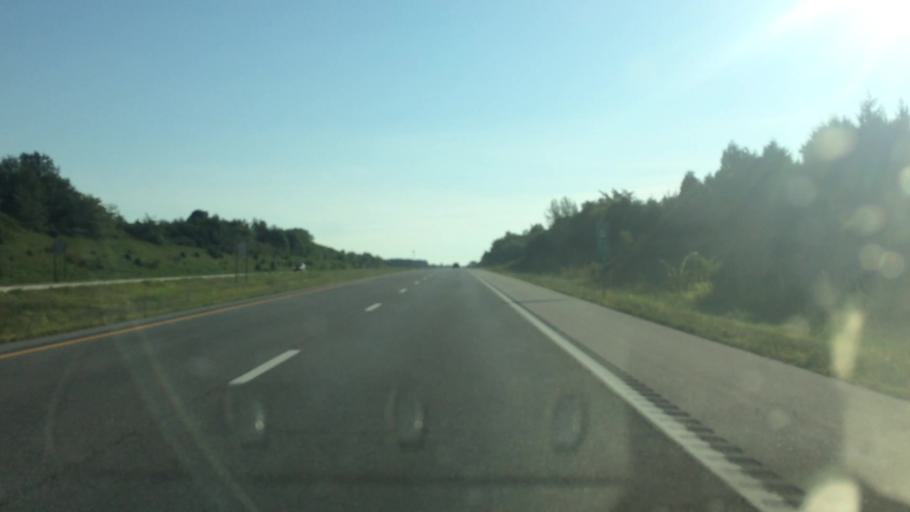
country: US
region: Missouri
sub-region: Greene County
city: Springfield
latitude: 37.2681
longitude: -93.2209
